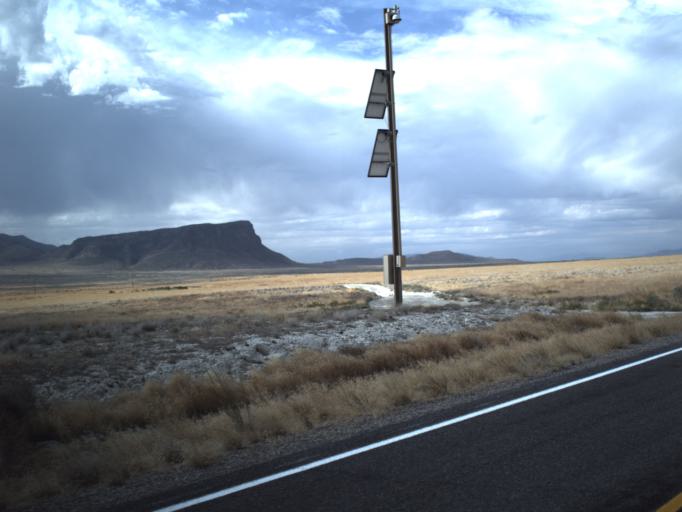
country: US
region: Utah
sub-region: Tooele County
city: Wendover
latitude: 41.3793
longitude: -113.9985
